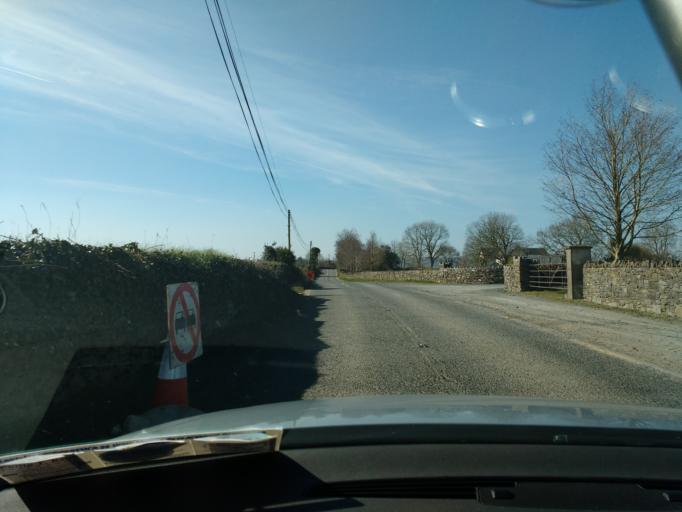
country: IE
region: Munster
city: Thurles
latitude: 52.6908
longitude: -7.8961
